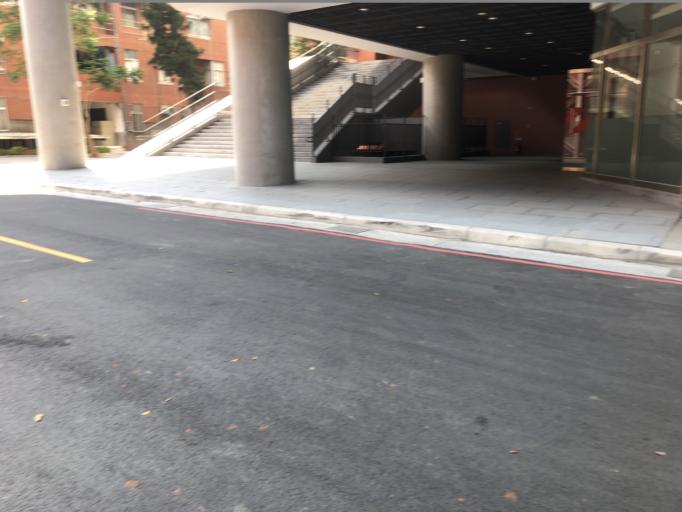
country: TW
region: Taiwan
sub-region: Tainan
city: Tainan
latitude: 23.0253
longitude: 120.2229
